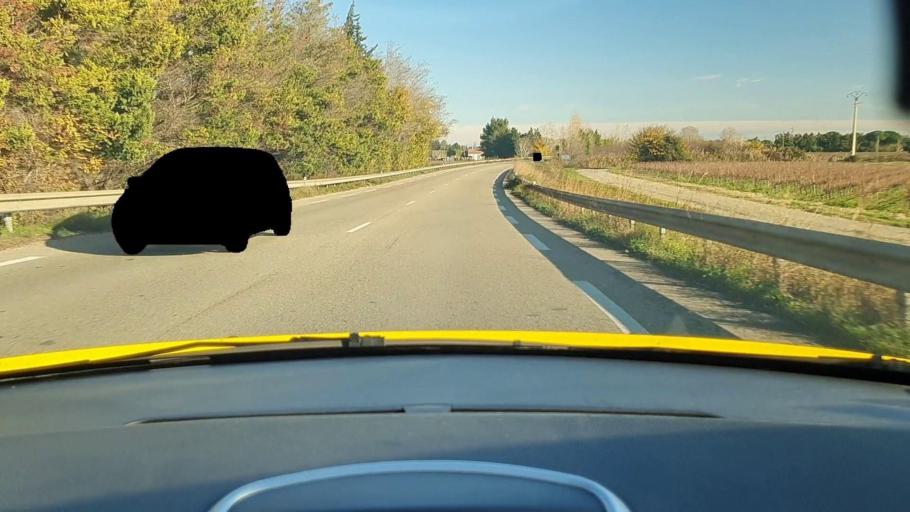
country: FR
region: Languedoc-Roussillon
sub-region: Departement du Gard
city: Beaucaire
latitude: 43.7935
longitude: 4.6223
